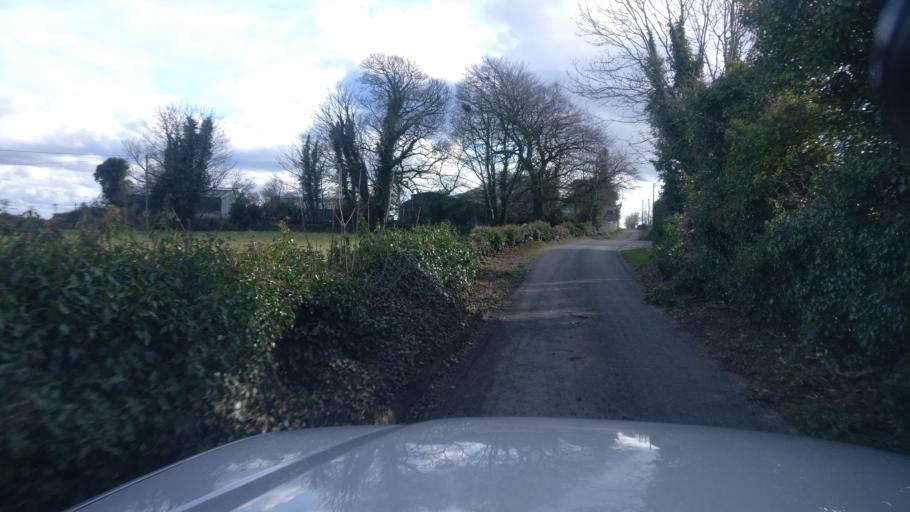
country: IE
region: Connaught
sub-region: County Galway
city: Loughrea
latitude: 53.1778
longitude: -8.4260
